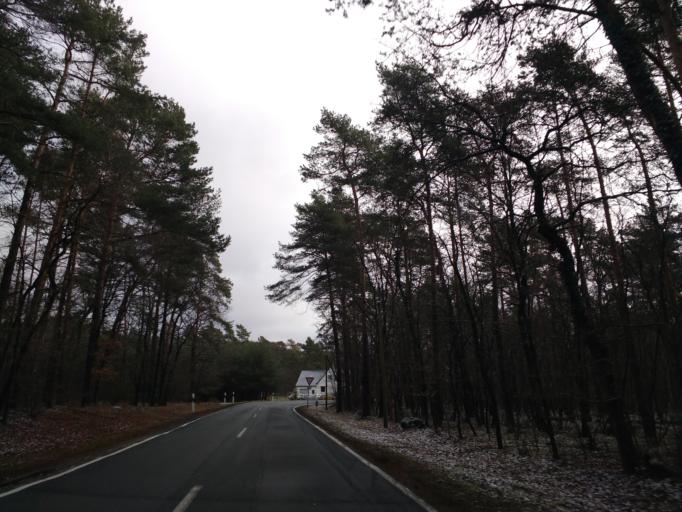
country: DE
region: North Rhine-Westphalia
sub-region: Regierungsbezirk Detmold
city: Augustdorf
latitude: 51.8707
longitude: 8.6958
